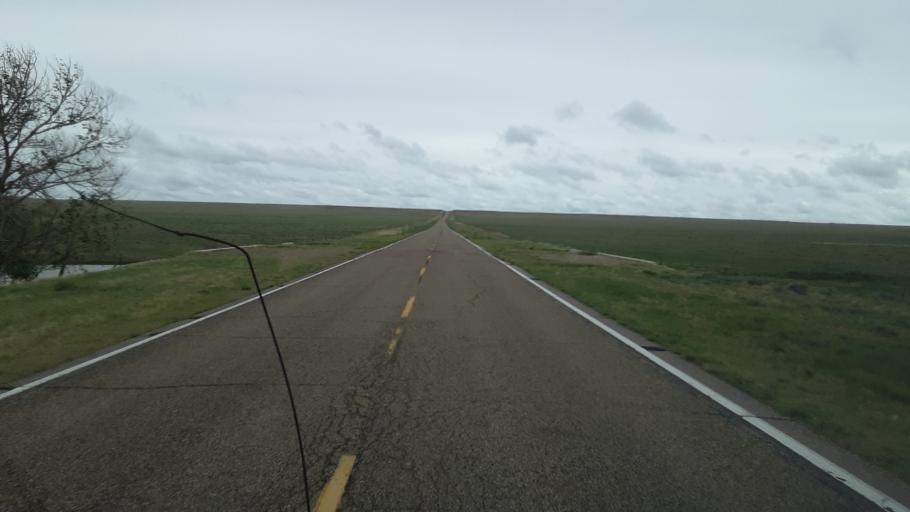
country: US
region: Colorado
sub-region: Lincoln County
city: Hugo
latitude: 38.8498
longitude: -103.3731
